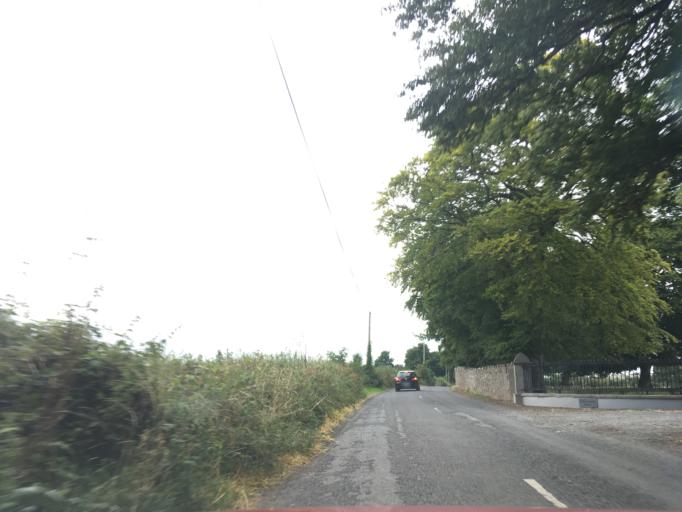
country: IE
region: Munster
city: Cahir
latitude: 52.4591
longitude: -7.9856
